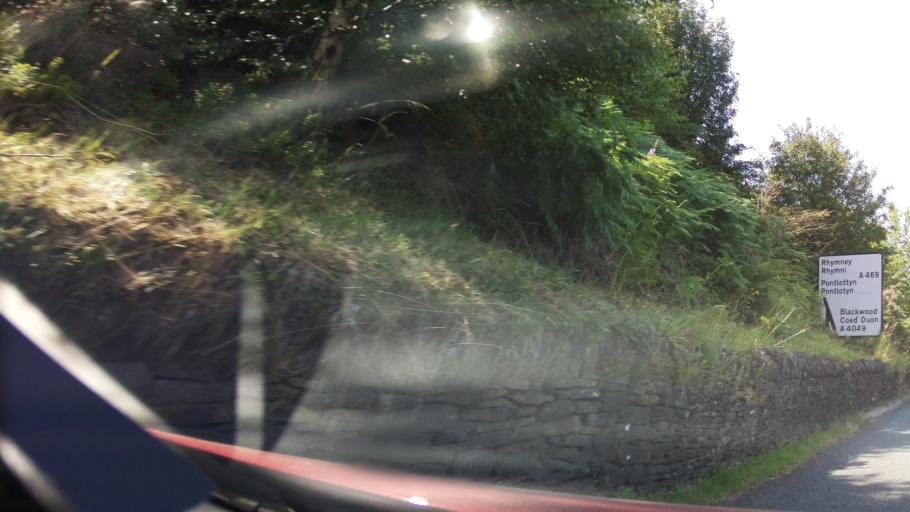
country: GB
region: Wales
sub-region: Caerphilly County Borough
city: New Tredegar
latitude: 51.7219
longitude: -3.2493
